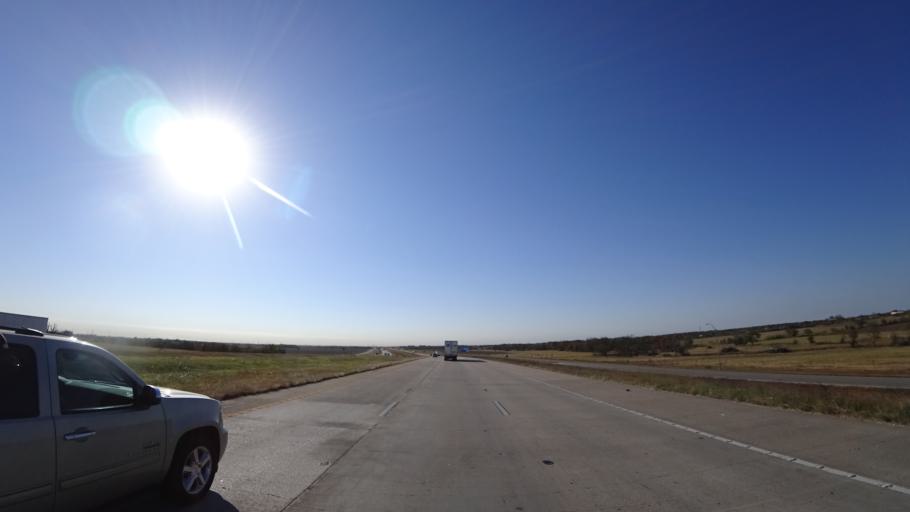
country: US
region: Texas
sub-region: Travis County
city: Pflugerville
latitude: 30.4505
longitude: -97.5945
